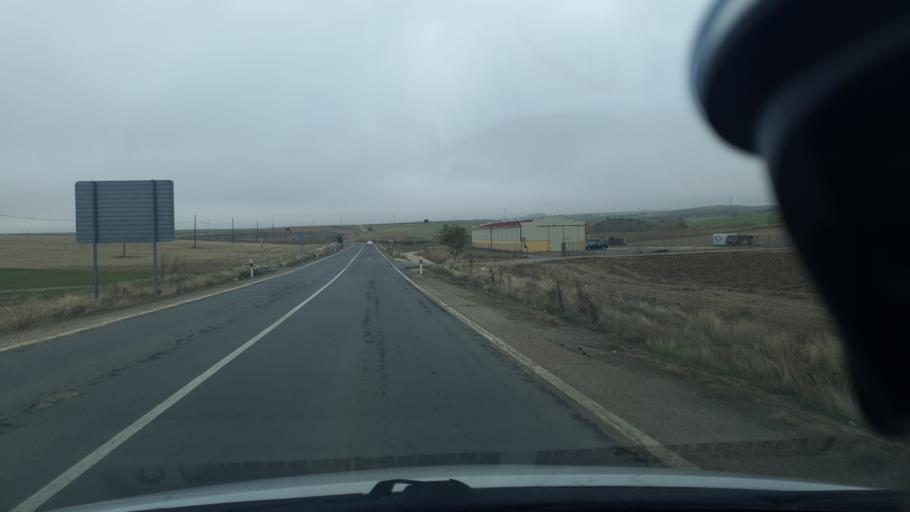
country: ES
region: Castille and Leon
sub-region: Provincia de Segovia
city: Encinillas
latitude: 41.0041
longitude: -4.1518
